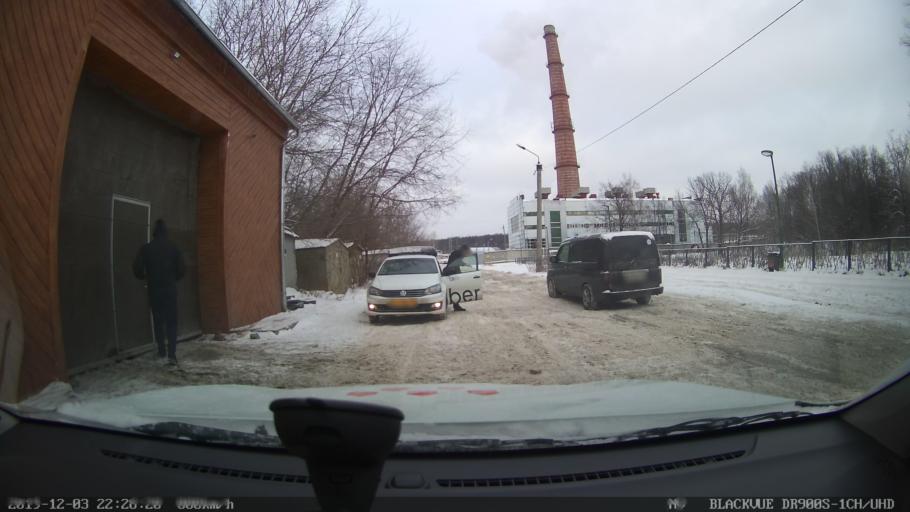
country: RU
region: Tatarstan
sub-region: Gorod Kazan'
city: Kazan
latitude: 55.7578
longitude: 49.2071
